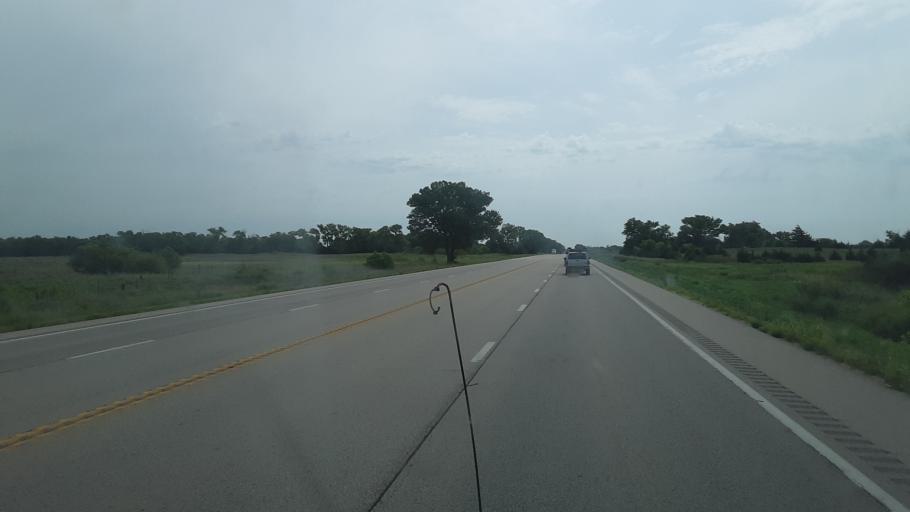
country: US
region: Kansas
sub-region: Rice County
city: Sterling
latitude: 37.9846
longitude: -98.2944
